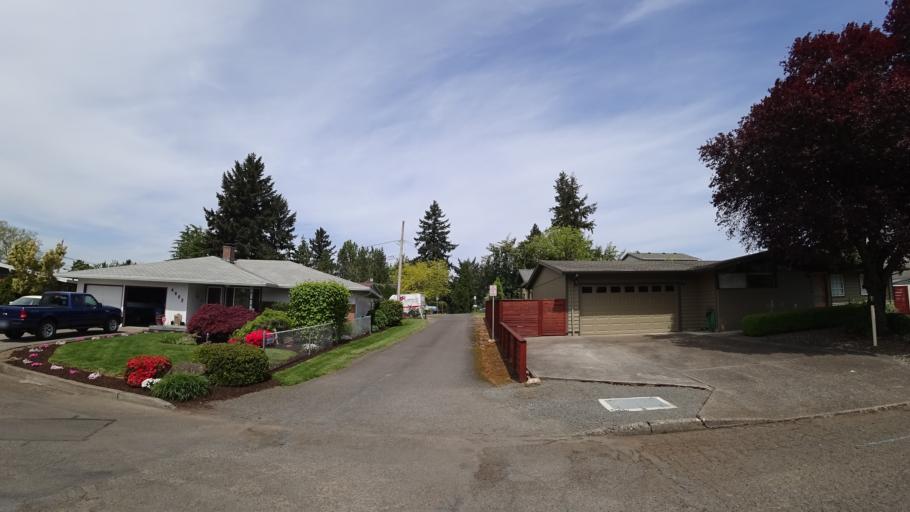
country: US
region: Oregon
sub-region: Clackamas County
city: Milwaukie
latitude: 45.4535
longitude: -122.6116
